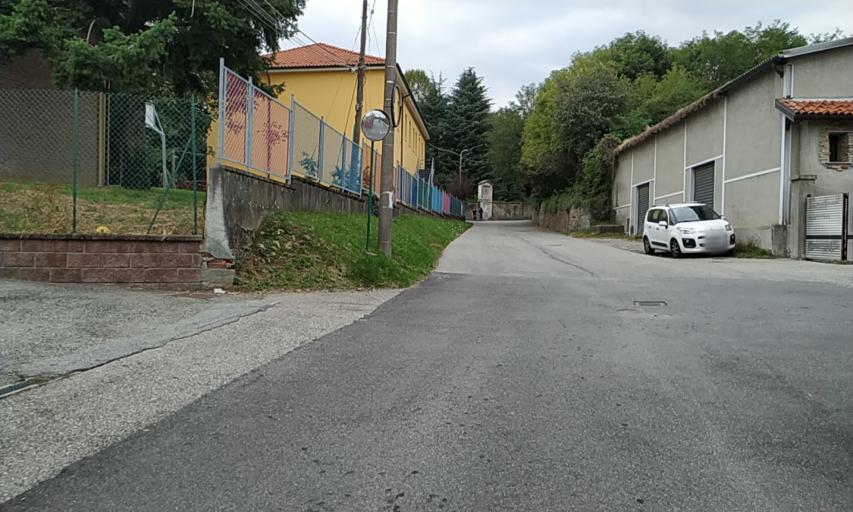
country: IT
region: Piedmont
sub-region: Provincia di Vercelli
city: Moncrivello
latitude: 45.3313
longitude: 7.9996
